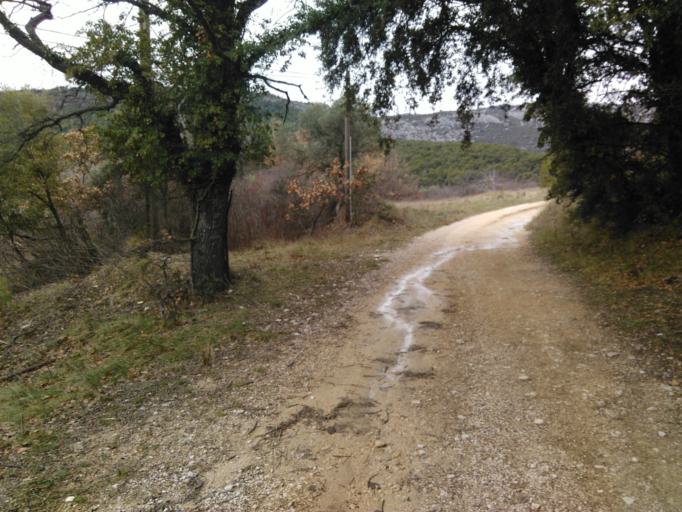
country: FR
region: Provence-Alpes-Cote d'Azur
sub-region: Departement du Vaucluse
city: Bedoin
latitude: 44.1365
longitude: 5.1581
